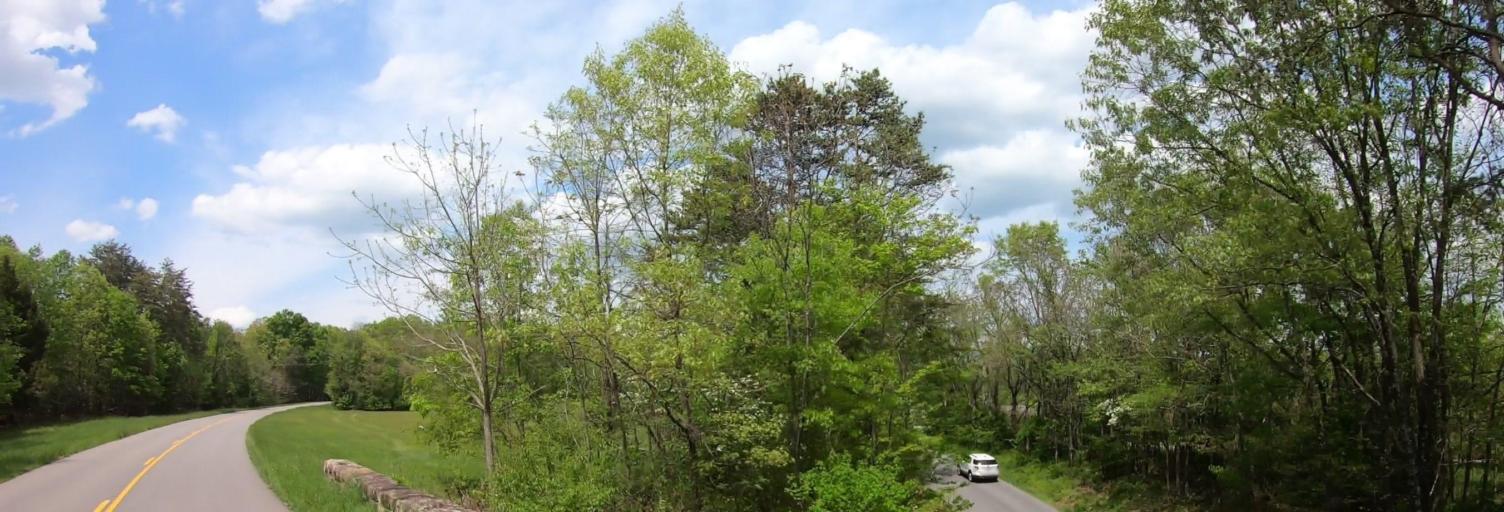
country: US
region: Virginia
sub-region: Botetourt County
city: Laymantown
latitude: 37.3705
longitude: -79.8393
